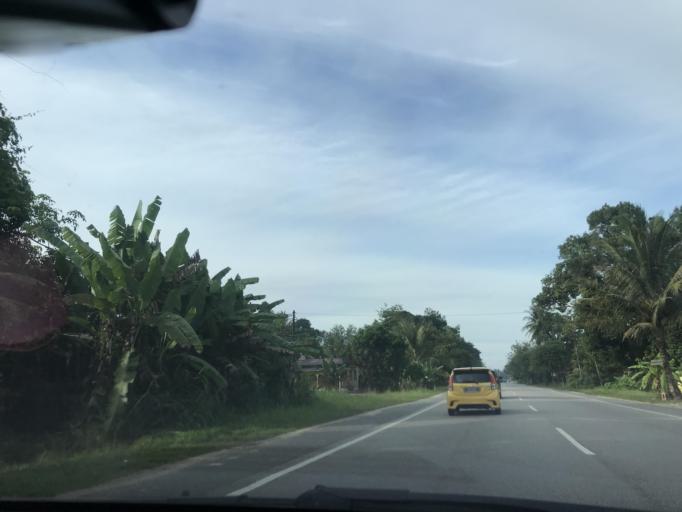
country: MY
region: Kelantan
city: Kampong Pangkal Kalong
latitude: 5.9629
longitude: 102.1938
